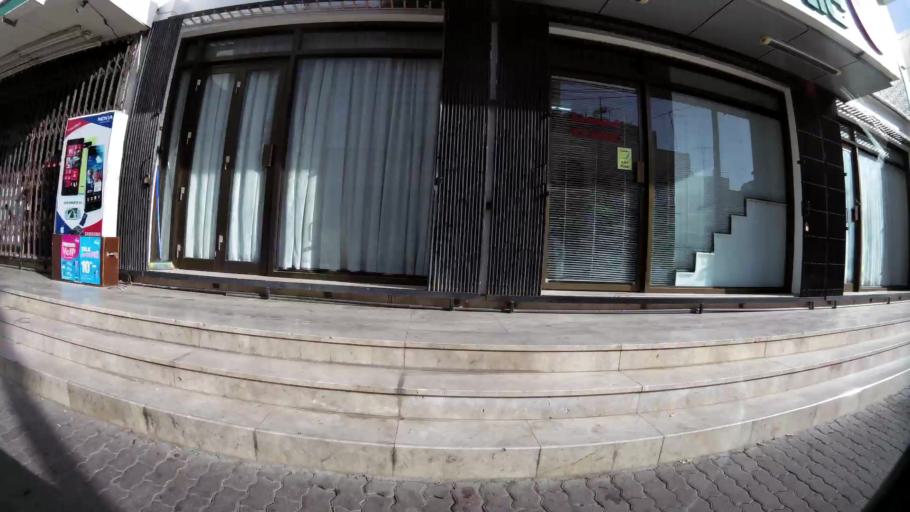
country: OM
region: Muhafazat Masqat
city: Muscat
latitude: 23.5904
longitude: 58.5445
